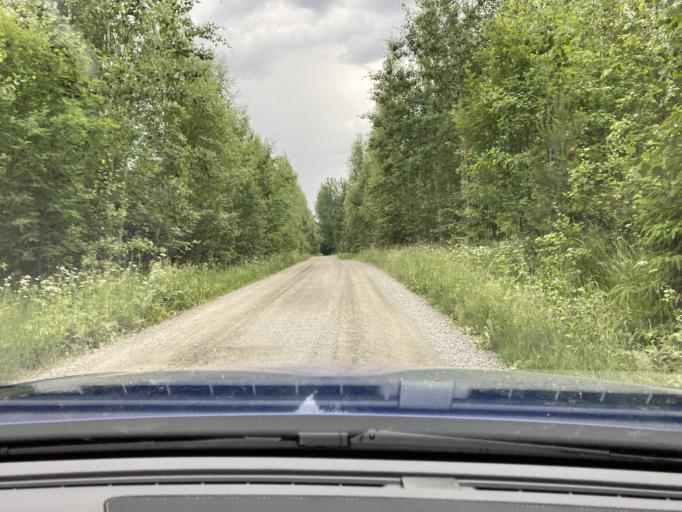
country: FI
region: Satakunta
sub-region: Rauma
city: Lappi
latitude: 61.1432
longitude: 21.9056
